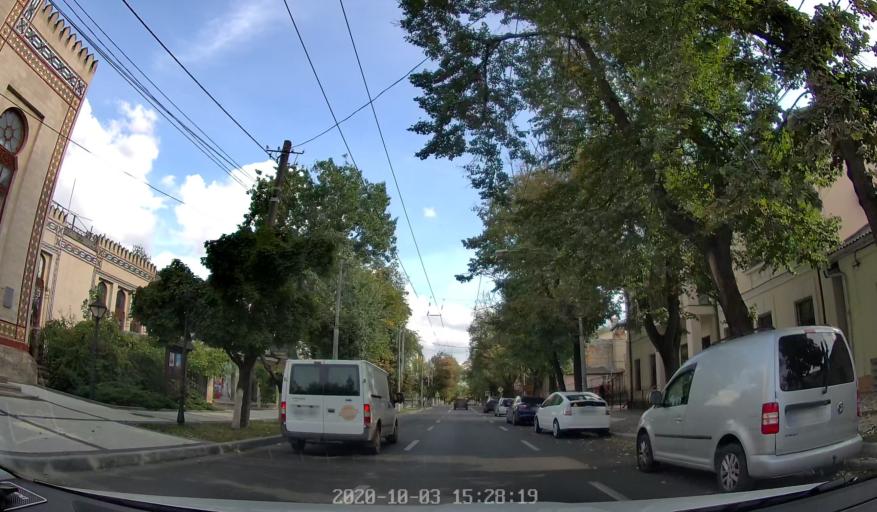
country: MD
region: Chisinau
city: Chisinau
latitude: 47.0232
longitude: 28.8197
